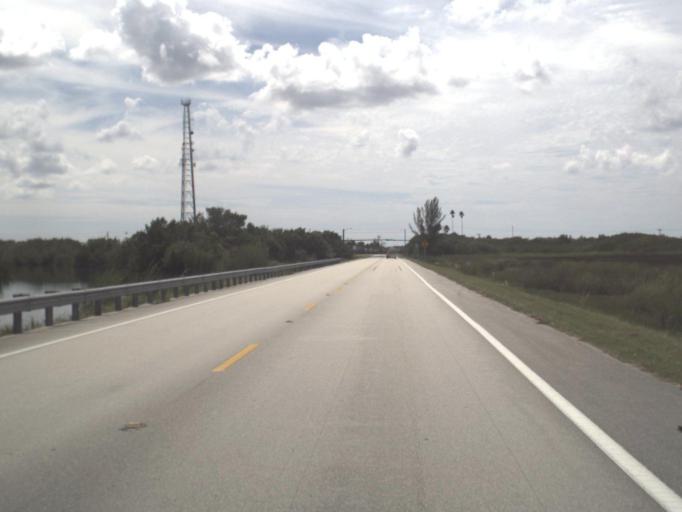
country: US
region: Florida
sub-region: Collier County
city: Marco
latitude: 25.9145
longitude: -81.3622
